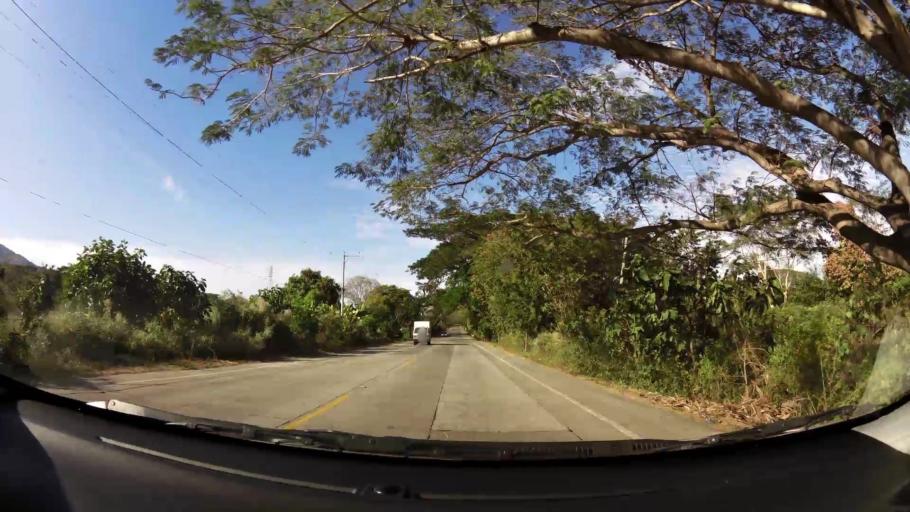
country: SV
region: Santa Ana
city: Texistepeque
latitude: 14.0956
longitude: -89.4996
